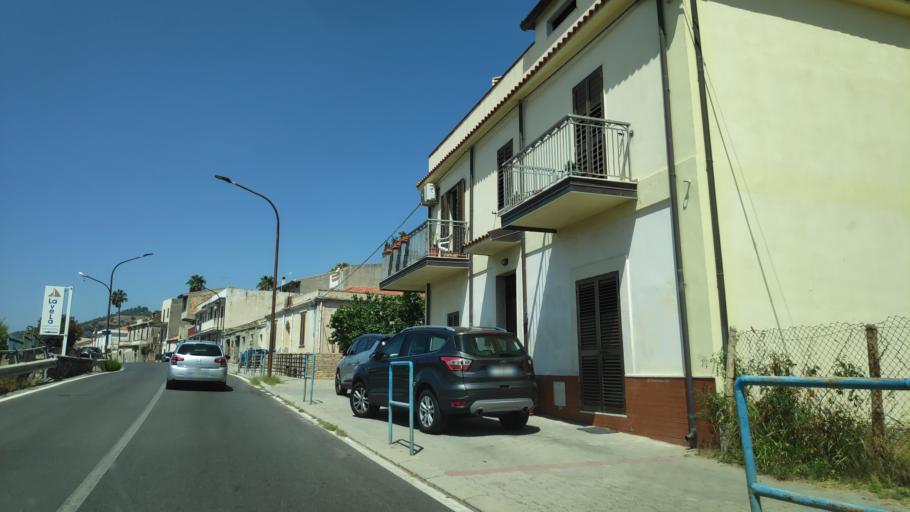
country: IT
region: Calabria
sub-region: Provincia di Reggio Calabria
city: Palizzi Marina
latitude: 37.9182
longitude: 15.9937
